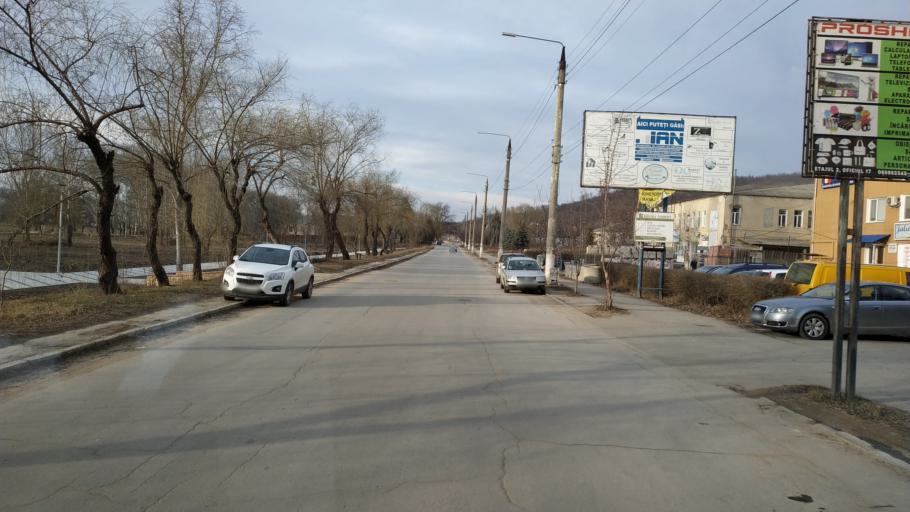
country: MD
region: Nisporeni
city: Nisporeni
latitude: 47.0832
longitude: 28.1825
